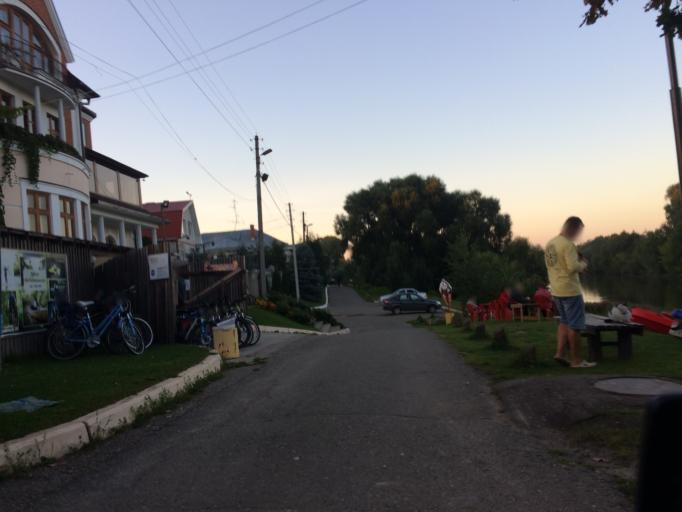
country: RU
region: Mariy-El
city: Yoshkar-Ola
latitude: 56.6405
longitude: 47.9057
